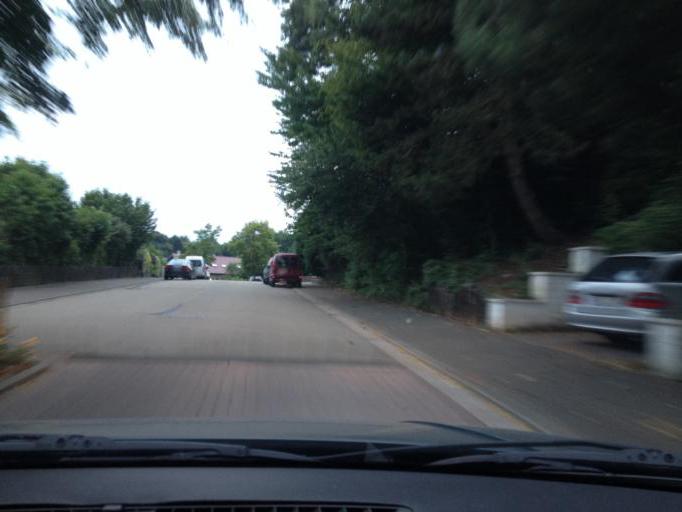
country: DE
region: Saarland
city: Sankt Wendel
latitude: 49.4748
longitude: 7.1517
